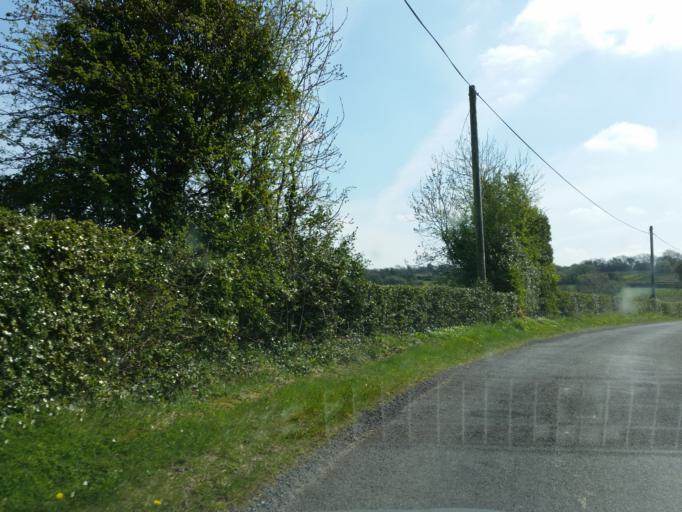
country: GB
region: Northern Ireland
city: Fivemiletown
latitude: 54.3117
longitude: -7.3608
